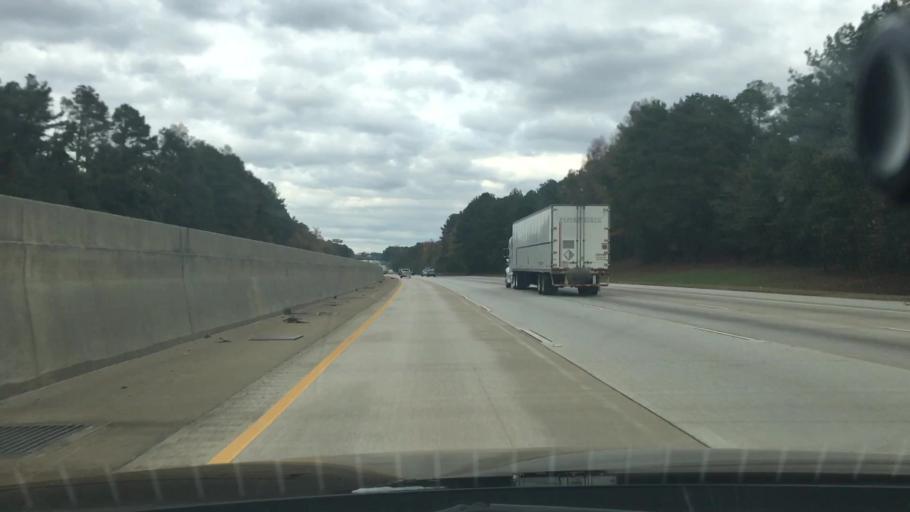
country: US
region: Georgia
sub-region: Fulton County
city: Fairburn
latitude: 33.5305
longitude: -84.6061
